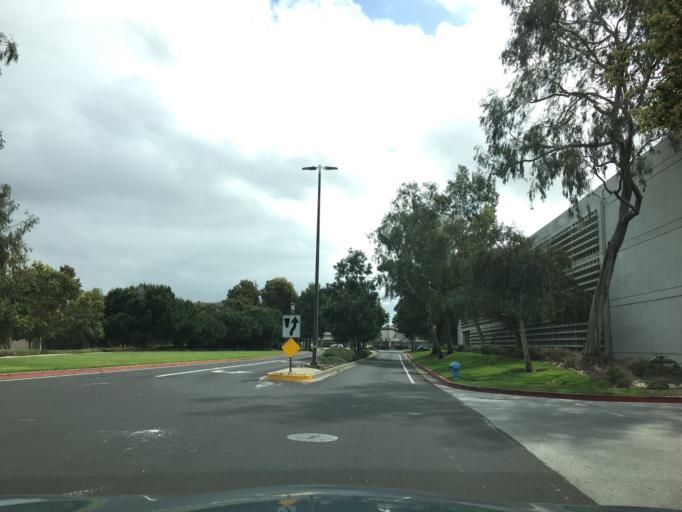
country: US
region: California
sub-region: San Mateo County
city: Redwood Shores
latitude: 37.5252
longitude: -122.2543
